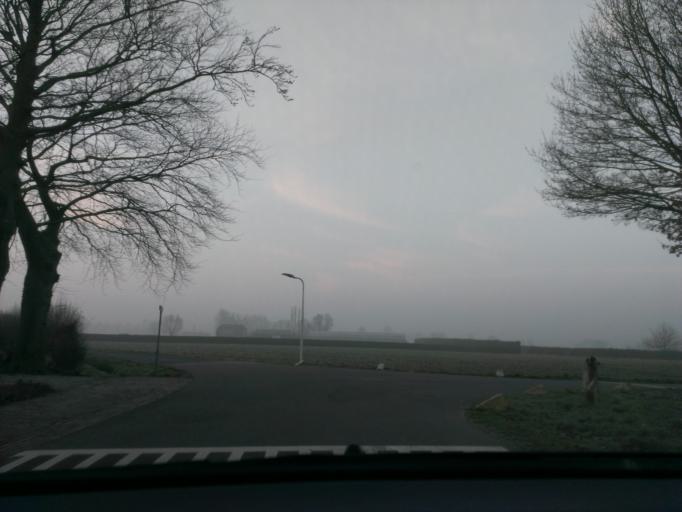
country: NL
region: Gelderland
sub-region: Gemeente Epe
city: Oene
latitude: 52.3419
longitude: 6.0440
